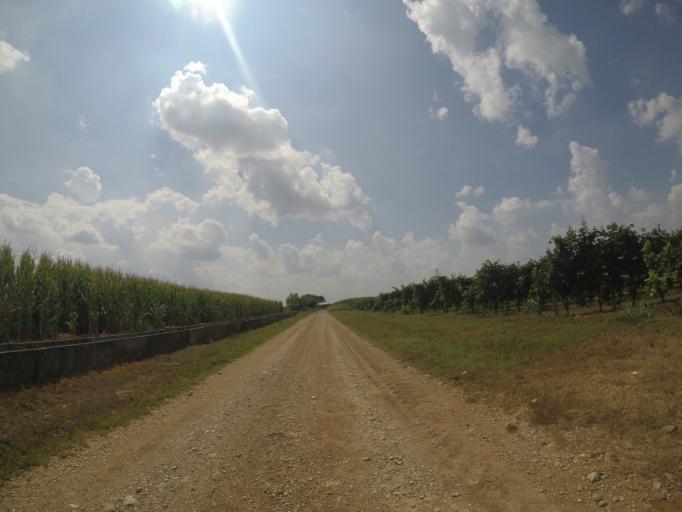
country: IT
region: Friuli Venezia Giulia
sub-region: Provincia di Udine
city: Bertiolo
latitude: 45.9562
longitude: 13.0481
